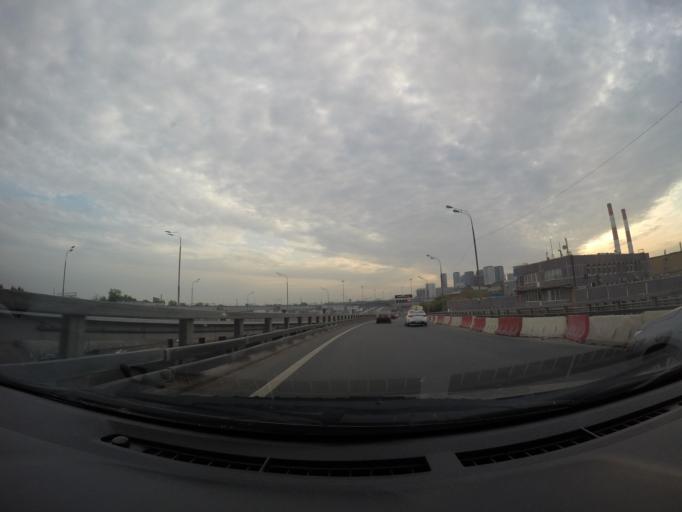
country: RU
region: Moscow
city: Tekstil'shchiki
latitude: 55.7236
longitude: 37.7103
